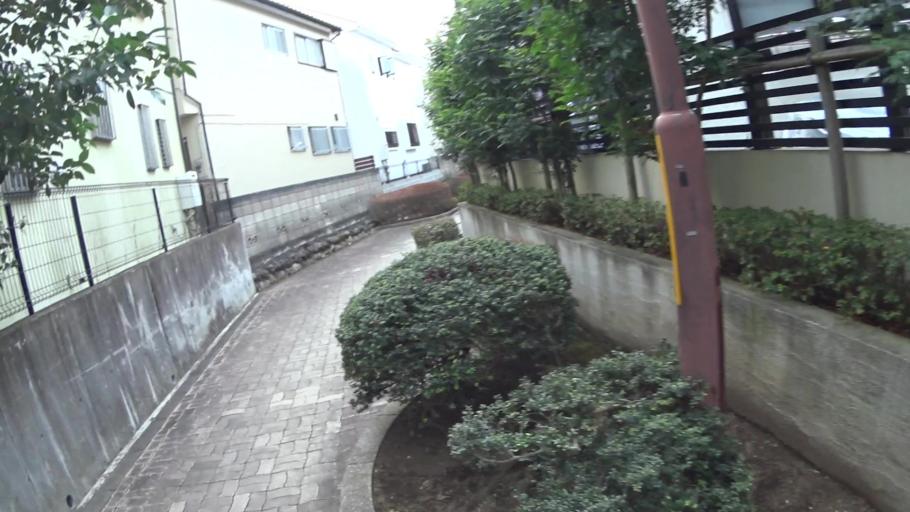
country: JP
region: Tokyo
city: Mitaka-shi
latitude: 35.6783
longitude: 139.5874
